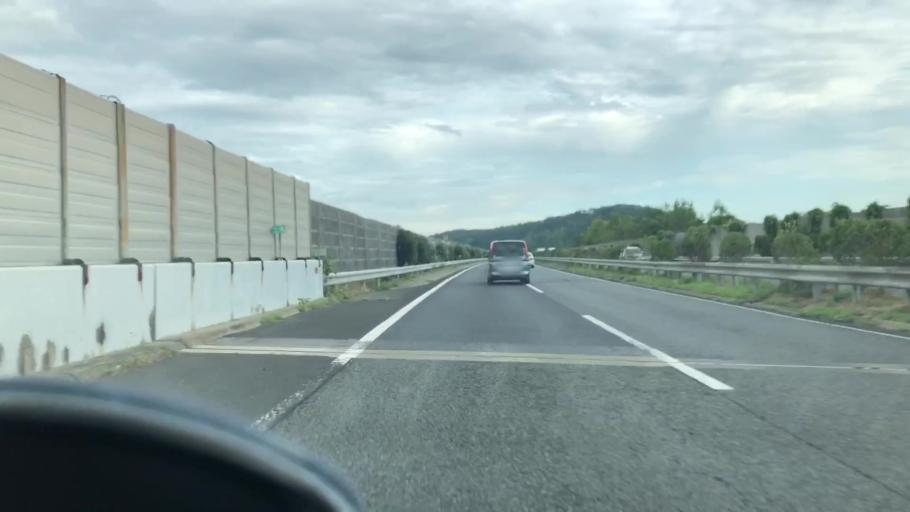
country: JP
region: Hyogo
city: Yashiro
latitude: 34.9056
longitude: 135.0648
